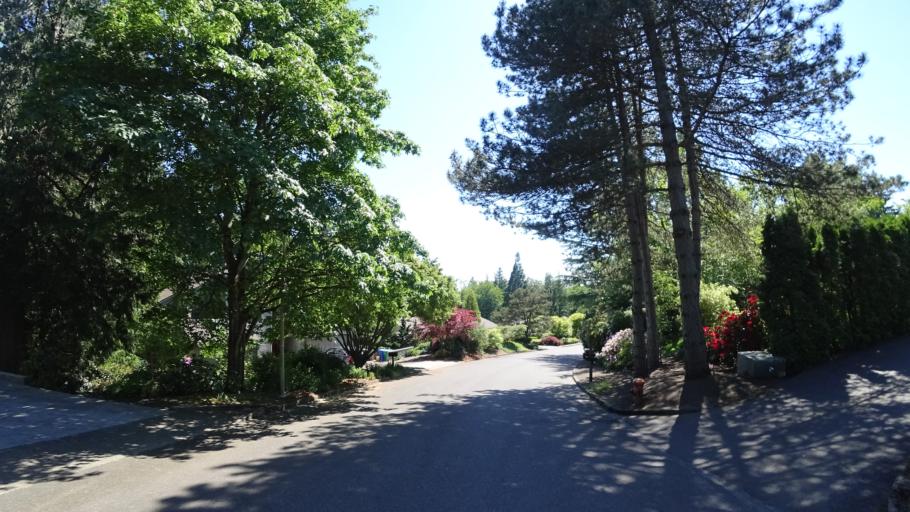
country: US
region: Oregon
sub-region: Washington County
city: West Slope
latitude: 45.4971
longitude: -122.7184
